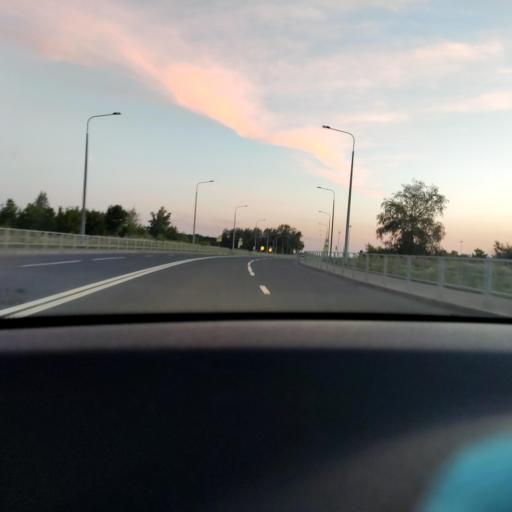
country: RU
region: Samara
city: Petra-Dubrava
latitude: 53.2918
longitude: 50.2398
